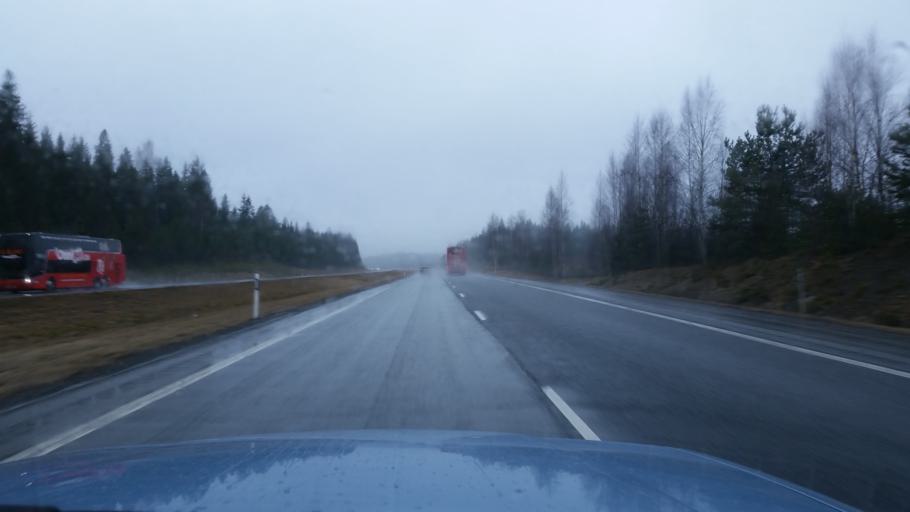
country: FI
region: Haeme
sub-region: Haemeenlinna
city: Kalvola
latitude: 61.1173
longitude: 24.1303
